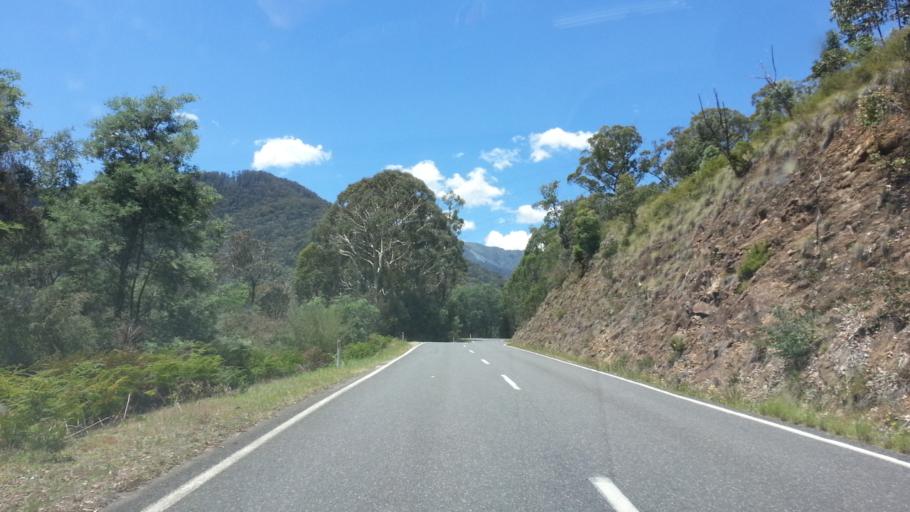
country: AU
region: Victoria
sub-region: Alpine
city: Mount Beauty
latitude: -36.7652
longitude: 147.2119
